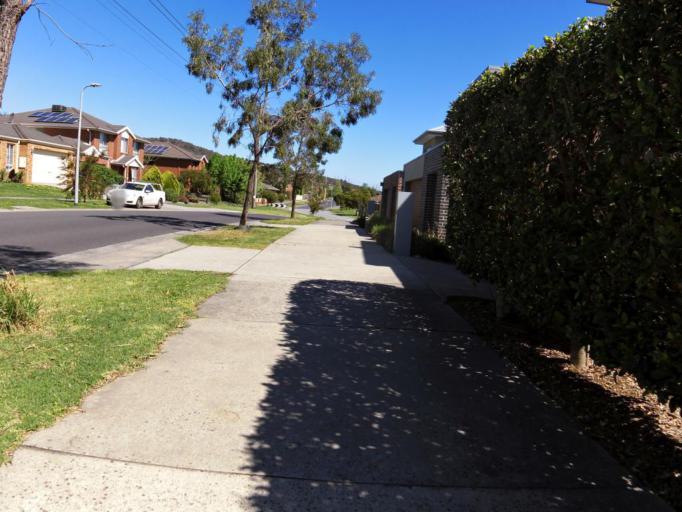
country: AU
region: Victoria
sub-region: Knox
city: Rowville
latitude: -37.9297
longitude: 145.2530
